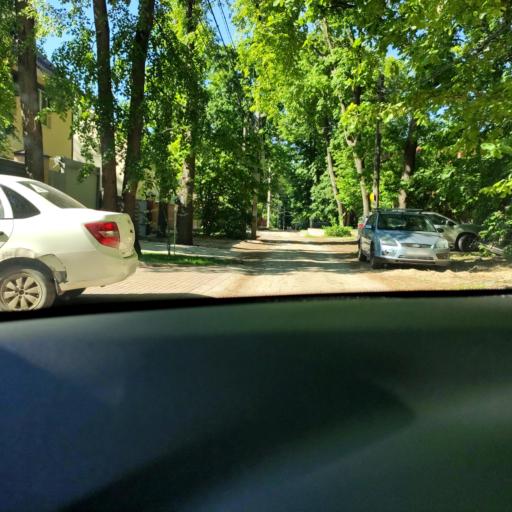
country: RU
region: Samara
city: Samara
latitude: 53.2943
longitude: 50.1978
